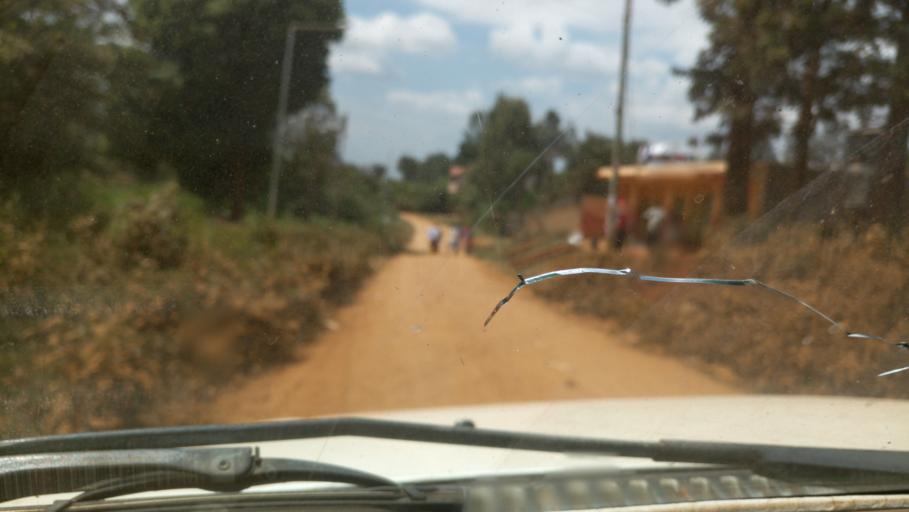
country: KE
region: Murang'a District
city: Murang'a
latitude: -0.7318
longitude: 37.1525
